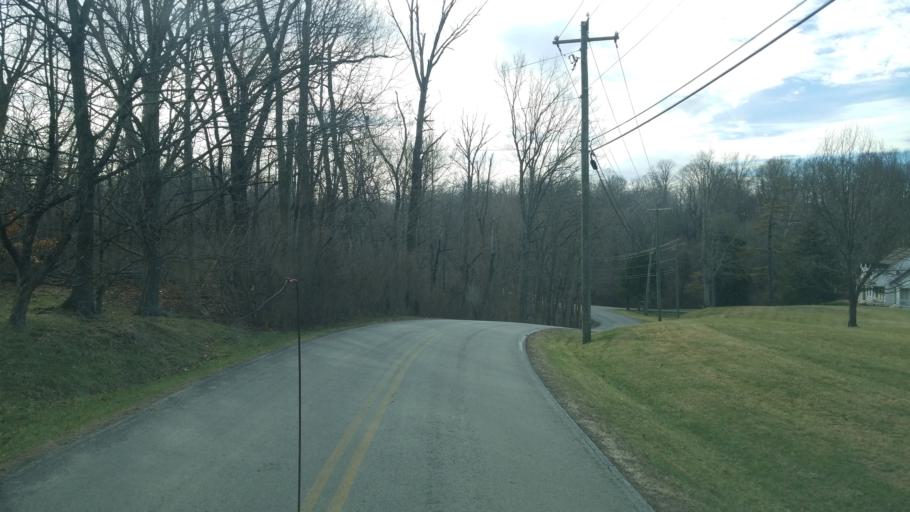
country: US
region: Ohio
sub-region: Warren County
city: Lebanon
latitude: 39.4277
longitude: -84.1594
